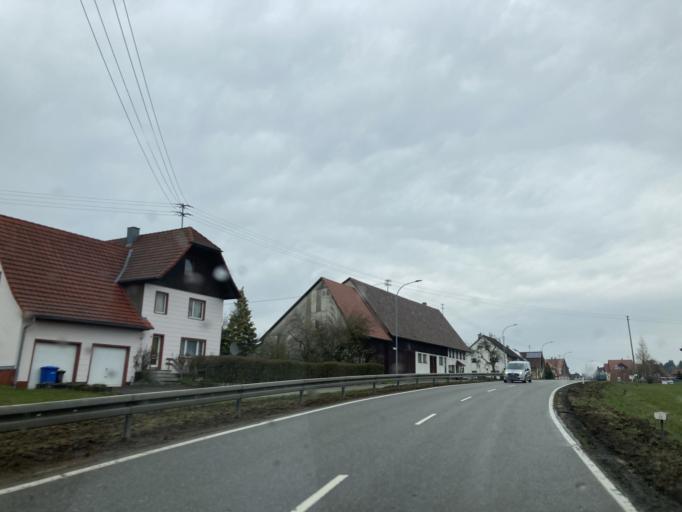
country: DE
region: Baden-Wuerttemberg
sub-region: Freiburg Region
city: Aichhalden
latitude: 48.2541
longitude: 8.4446
